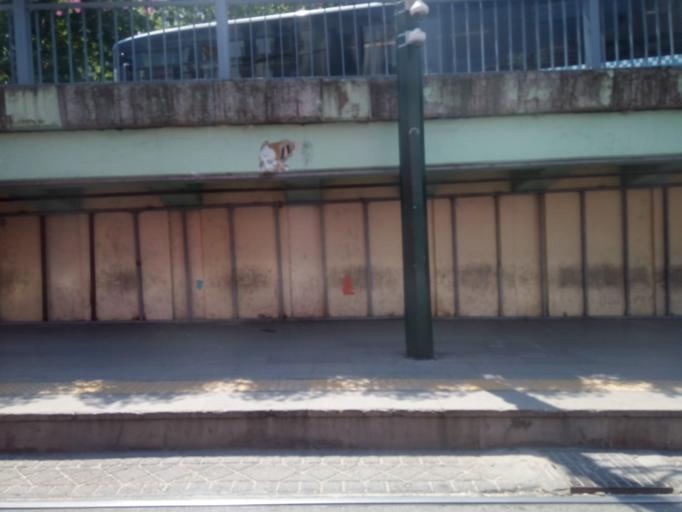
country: TR
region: Istanbul
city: Istanbul
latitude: 41.0098
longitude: 28.9544
